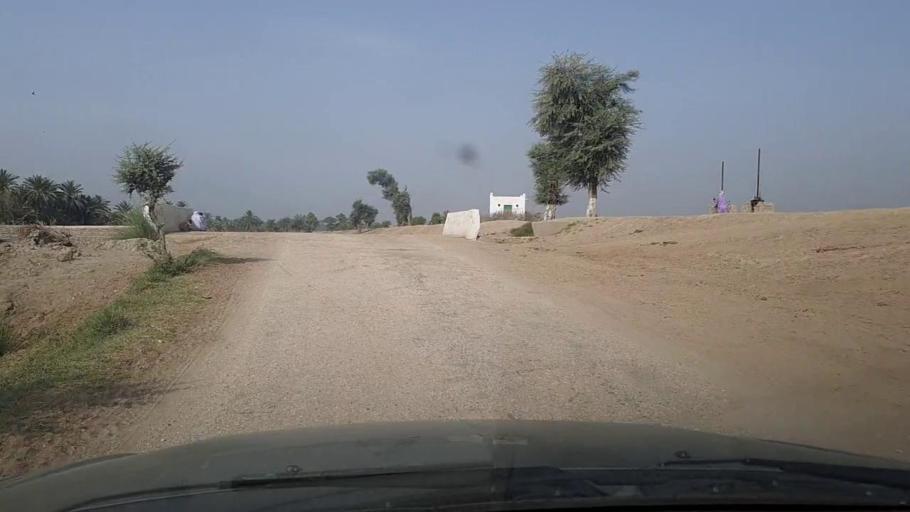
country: PK
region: Sindh
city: Pir jo Goth
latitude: 27.5332
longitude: 68.5080
